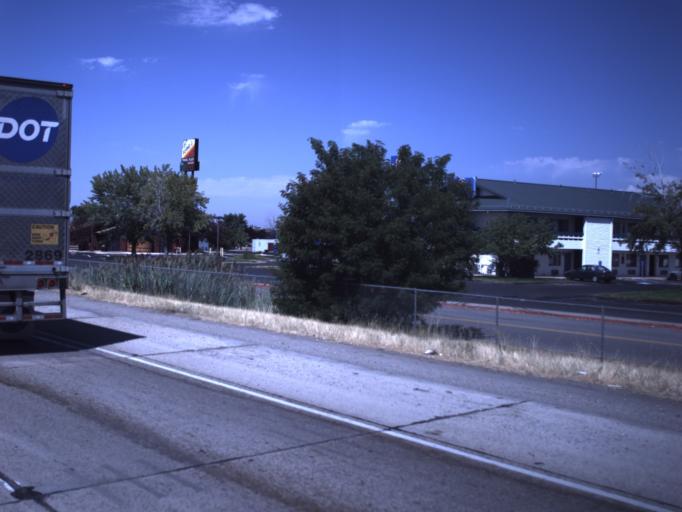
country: US
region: Utah
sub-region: Weber County
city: Marriott-Slaterville
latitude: 41.2293
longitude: -112.0084
